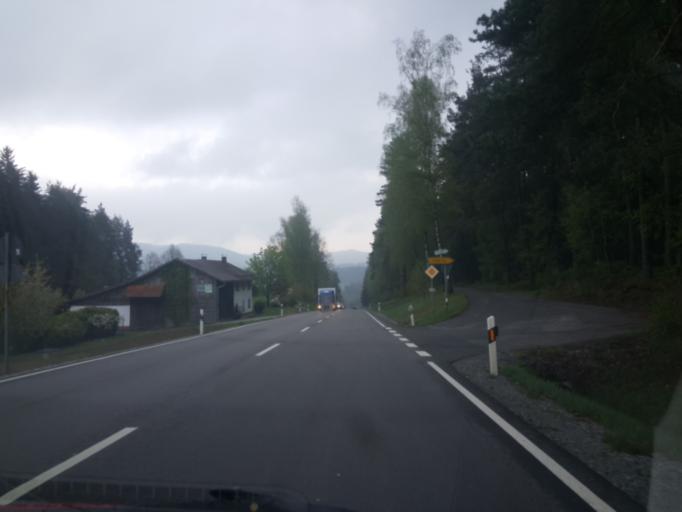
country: DE
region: Bavaria
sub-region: Lower Bavaria
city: Viechtach
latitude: 49.0621
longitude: 12.9040
